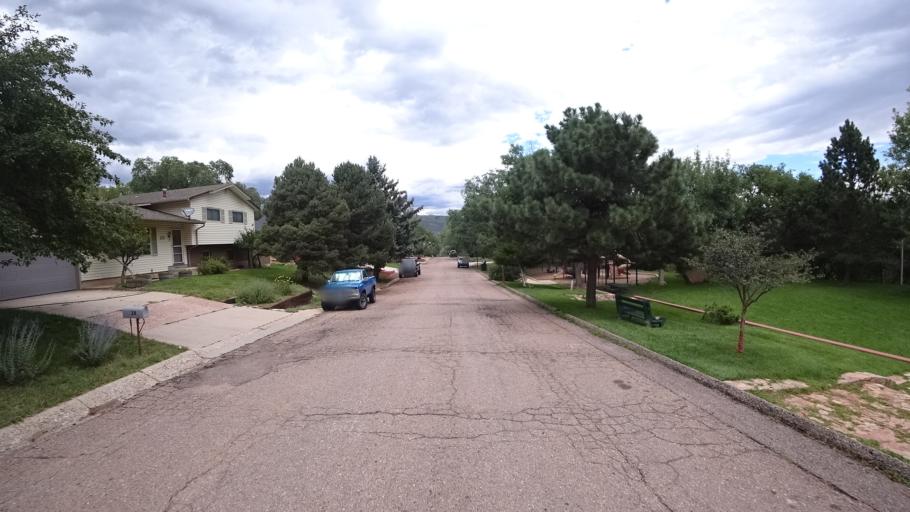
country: US
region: Colorado
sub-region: El Paso County
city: Manitou Springs
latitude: 38.8503
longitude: -104.8917
